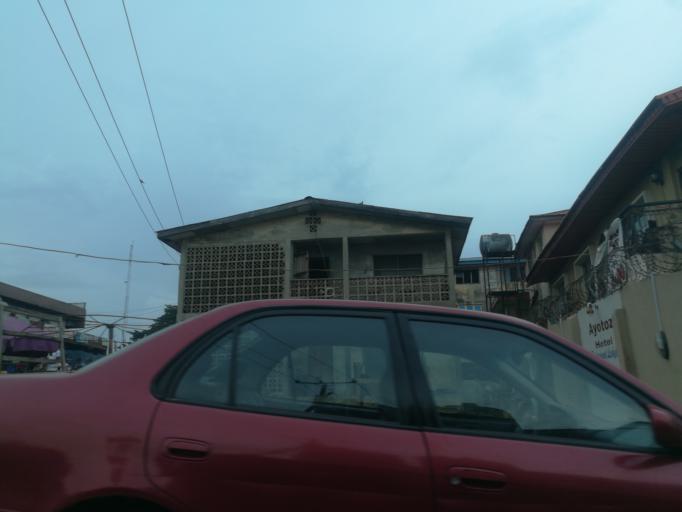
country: NG
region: Oyo
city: Ibadan
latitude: 7.4415
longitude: 3.9075
